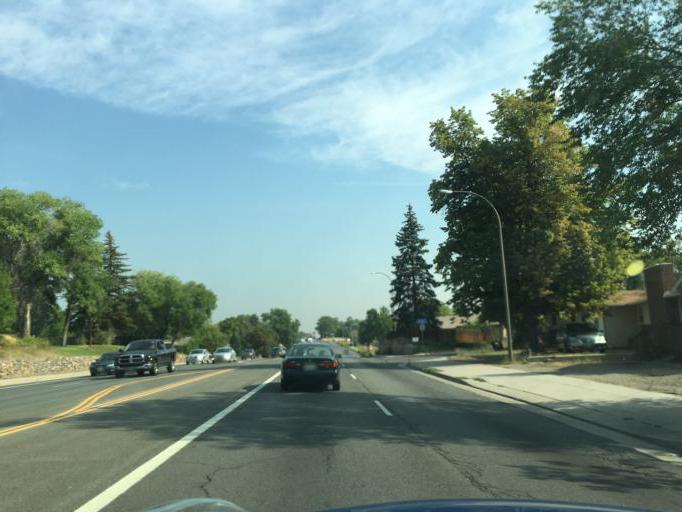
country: US
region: Colorado
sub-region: Jefferson County
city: Wheat Ridge
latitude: 39.7509
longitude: -105.0814
